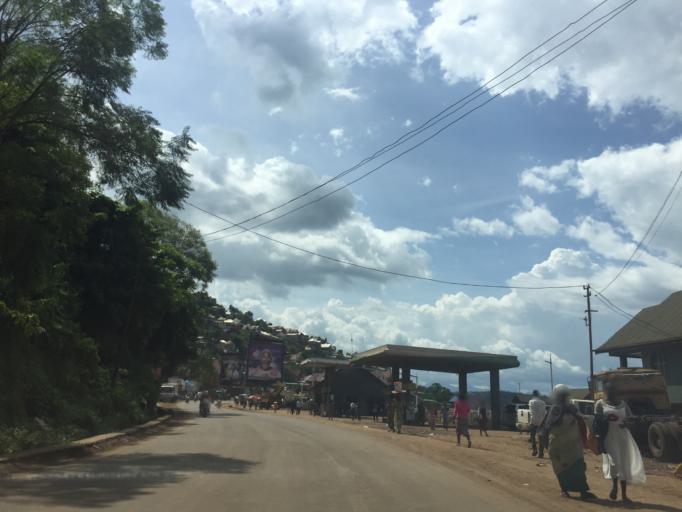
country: CD
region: South Kivu
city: Bukavu
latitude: -2.4895
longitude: 28.8486
